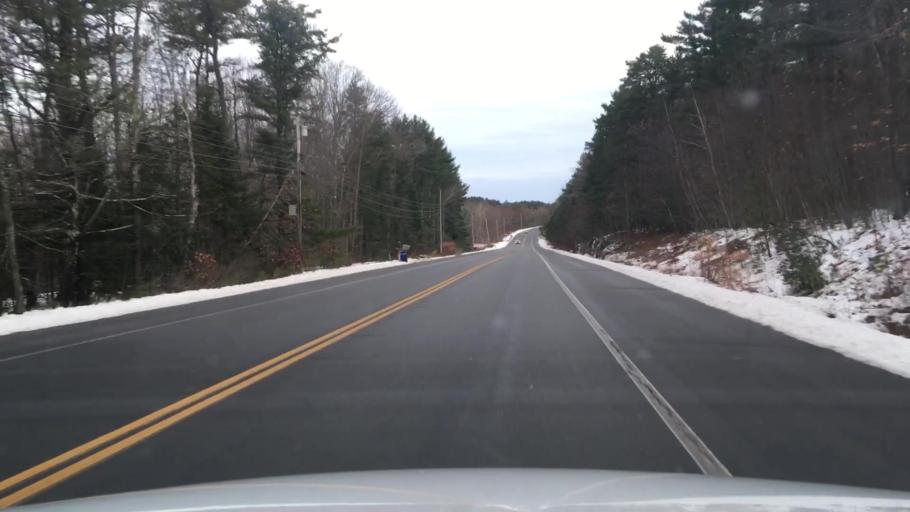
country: US
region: Maine
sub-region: Cumberland County
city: Falmouth Foreside
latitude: 43.7592
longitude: -70.2072
